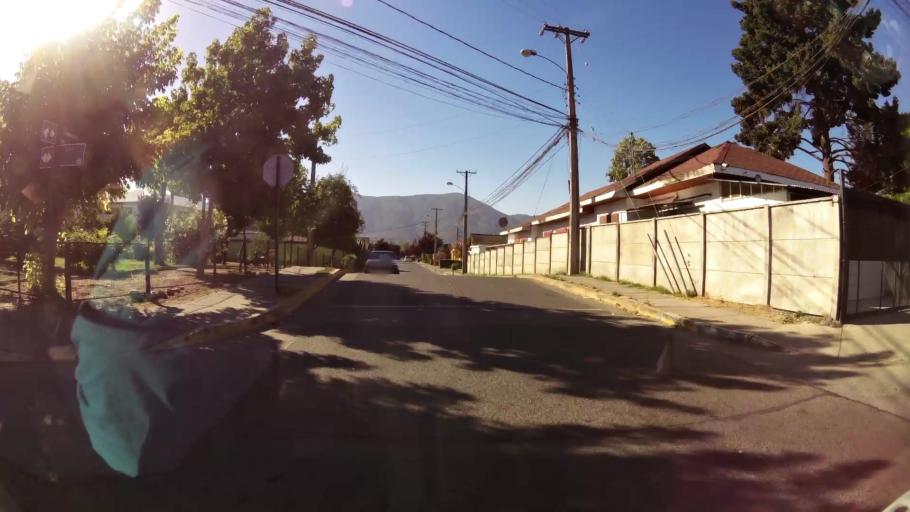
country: CL
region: O'Higgins
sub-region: Provincia de Colchagua
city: Chimbarongo
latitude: -34.5823
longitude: -70.9836
